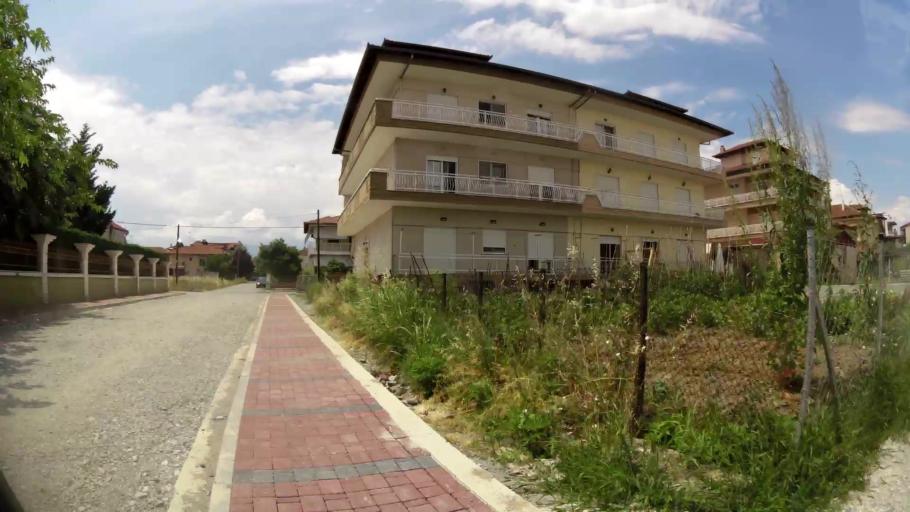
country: GR
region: Central Macedonia
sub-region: Nomos Pierias
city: Katerini
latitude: 40.2649
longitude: 22.5191
